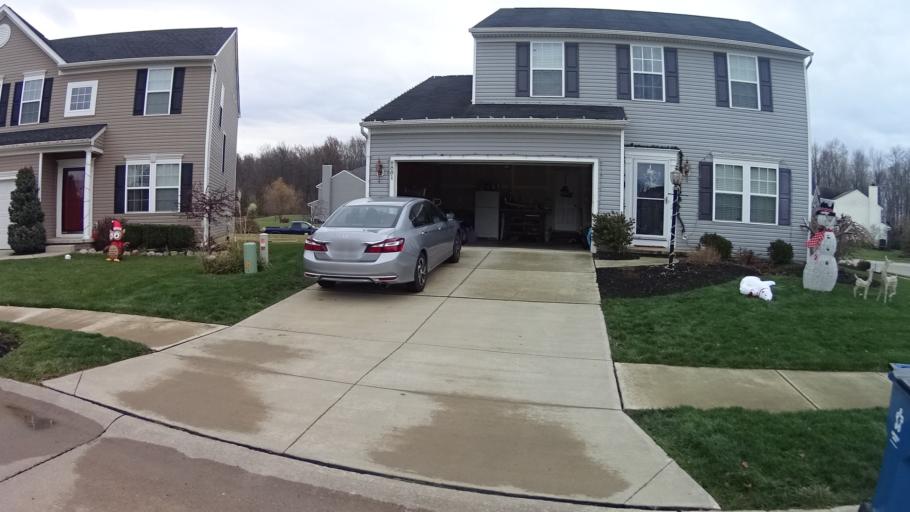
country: US
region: Ohio
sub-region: Lorain County
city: North Ridgeville
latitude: 41.3641
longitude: -82.0375
